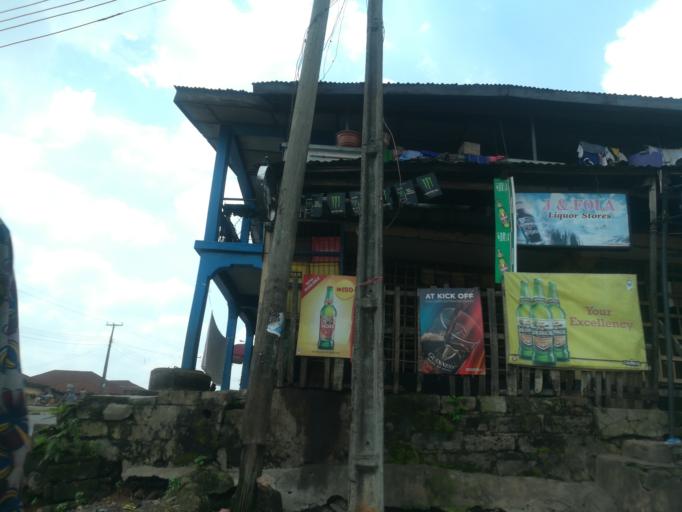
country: NG
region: Oyo
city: Ibadan
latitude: 7.3893
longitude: 3.9036
